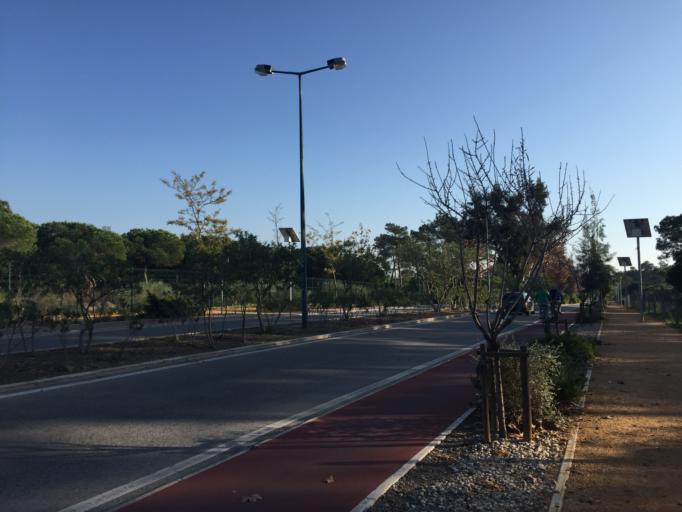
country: PT
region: Faro
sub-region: Vila Real de Santo Antonio
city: Vila Real de Santo Antonio
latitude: 37.1905
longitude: -7.4239
